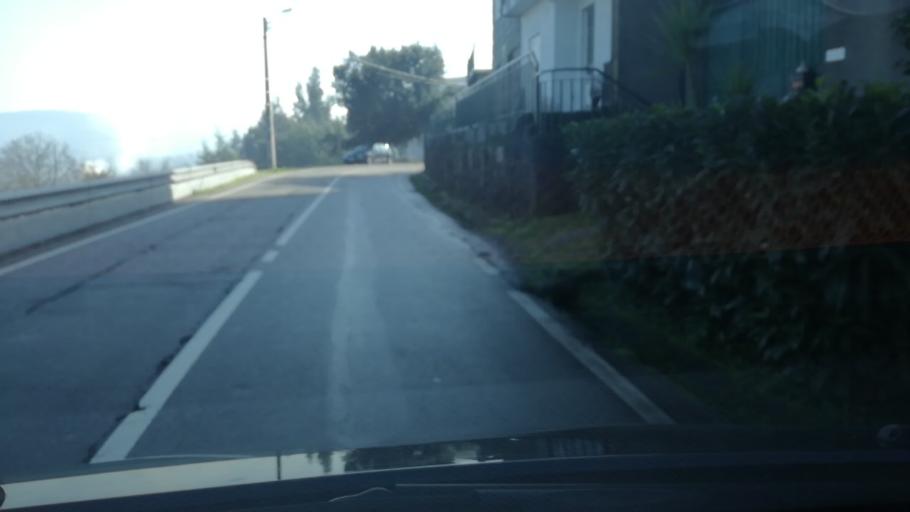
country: PT
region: Braga
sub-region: Guimaraes
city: Ponte
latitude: 41.5201
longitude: -8.3369
